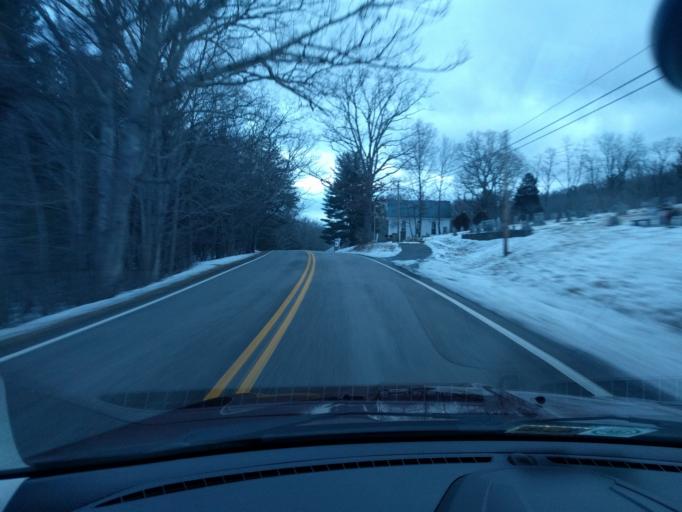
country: US
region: Virginia
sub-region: Alleghany County
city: Clifton Forge
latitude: 37.9288
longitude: -79.8839
